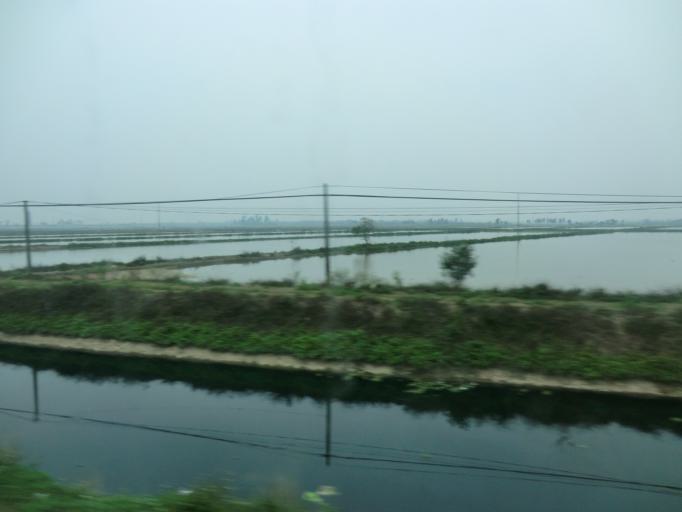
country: VN
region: Nam Dinh
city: Thi Tran Lam
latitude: 20.2945
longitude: 106.0238
